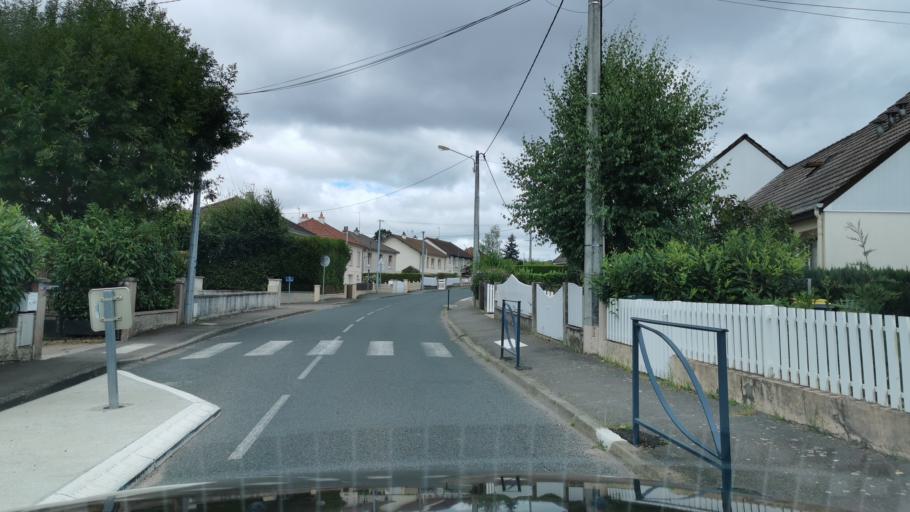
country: FR
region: Bourgogne
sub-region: Departement de Saone-et-Loire
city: Le Breuil
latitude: 46.8033
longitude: 4.4703
